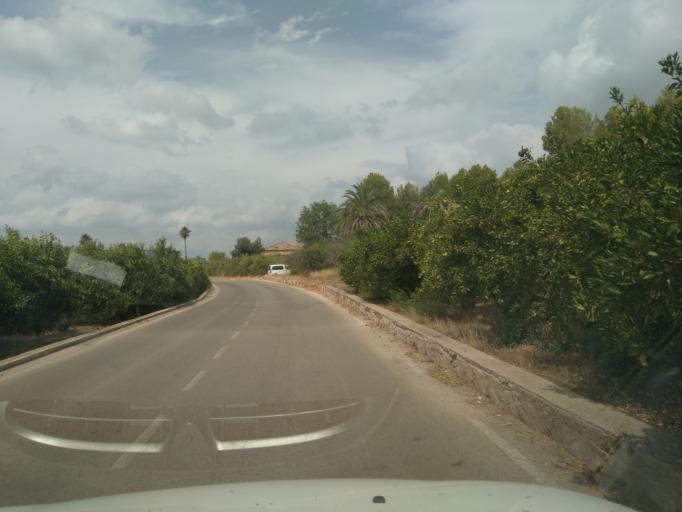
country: ES
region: Valencia
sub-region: Provincia de Valencia
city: La Pobla Llarga
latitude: 39.0865
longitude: -0.4237
